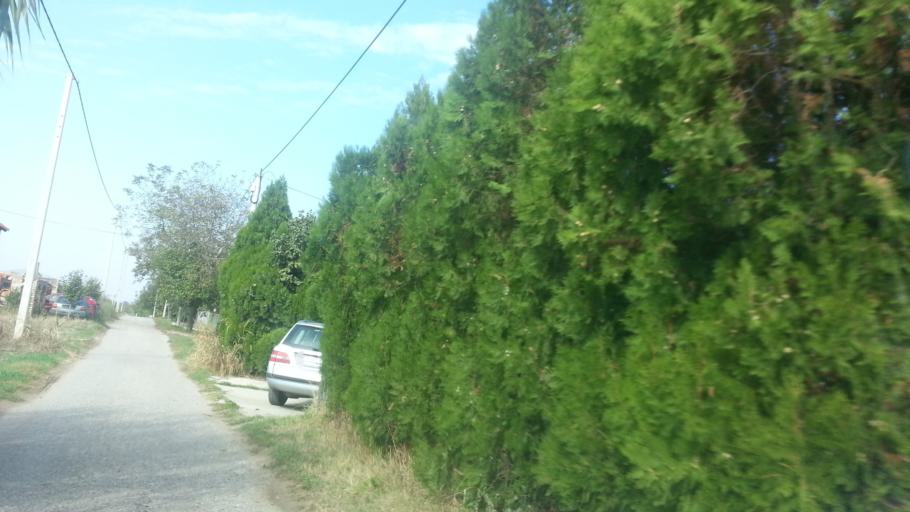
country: RS
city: Surduk
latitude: 45.0757
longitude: 20.3249
